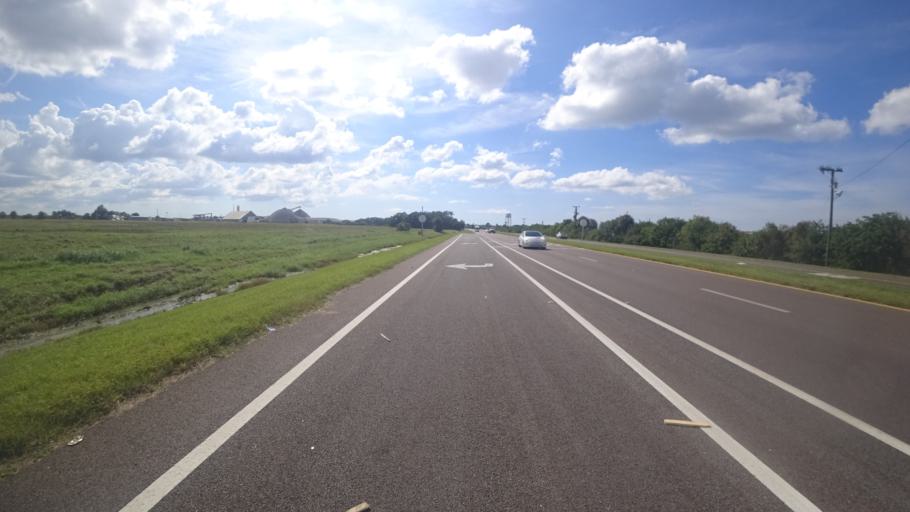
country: US
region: Florida
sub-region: Manatee County
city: Memphis
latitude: 27.6399
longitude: -82.5329
